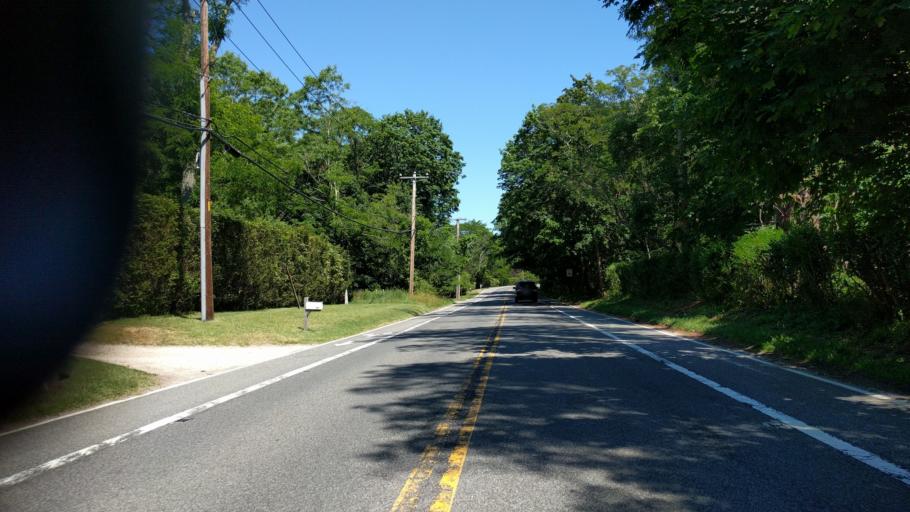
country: US
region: New York
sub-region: Suffolk County
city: Sag Harbor
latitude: 41.0123
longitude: -72.3100
